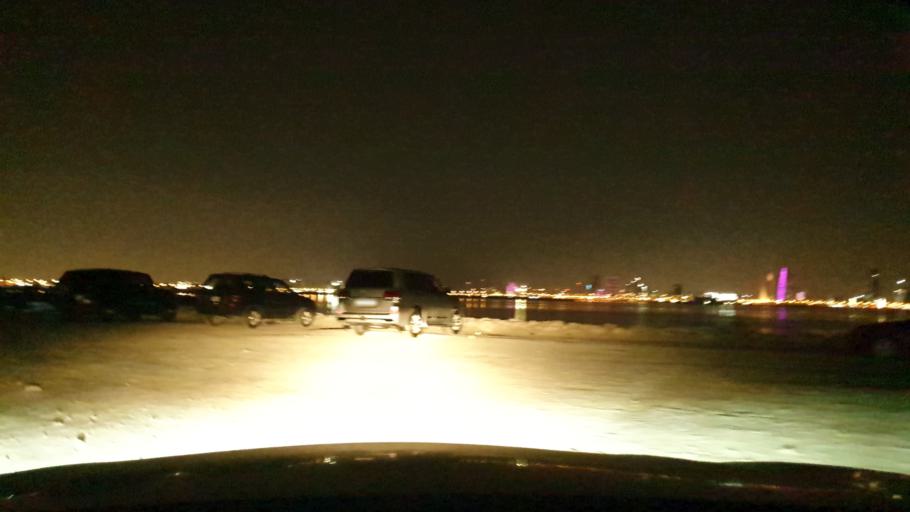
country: BH
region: Muharraq
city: Al Muharraq
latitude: 26.2841
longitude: 50.5777
